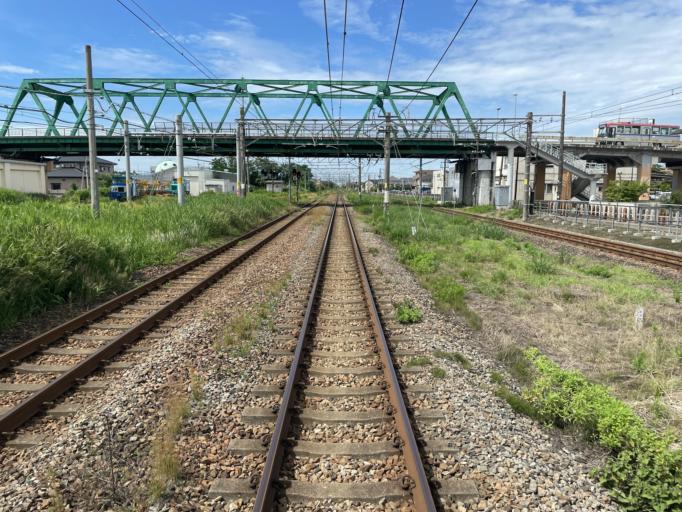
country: JP
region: Niigata
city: Shibata
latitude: 37.9425
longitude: 139.3336
